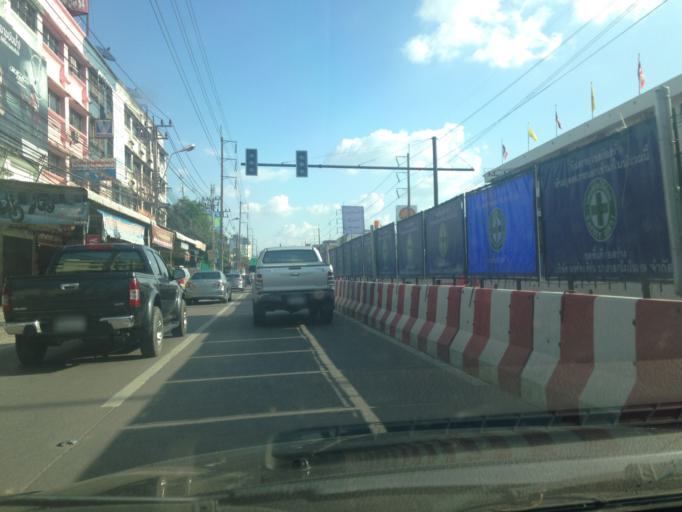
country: TH
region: Nonthaburi
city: Mueang Nonthaburi
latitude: 13.8826
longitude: 100.5132
